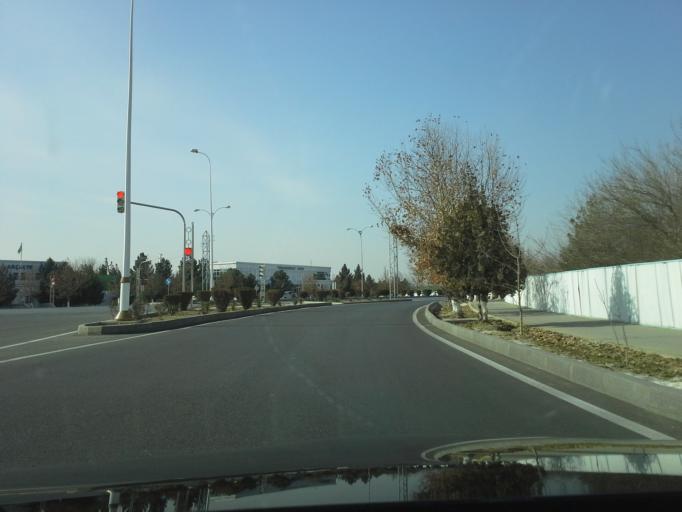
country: TM
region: Ahal
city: Abadan
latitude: 38.0516
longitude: 58.1852
